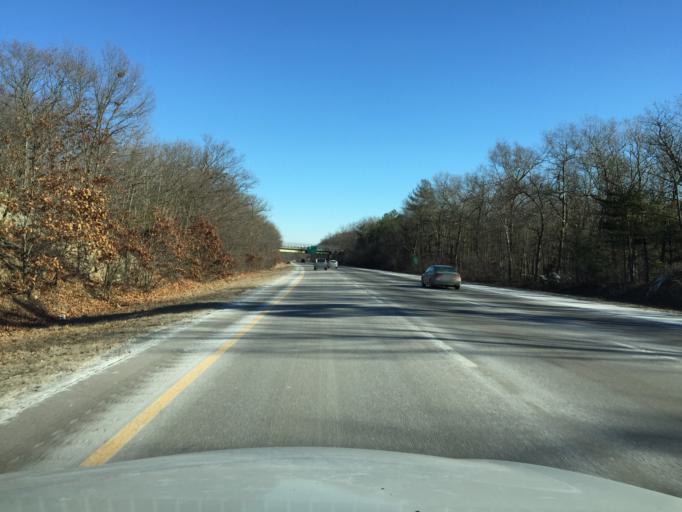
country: US
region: Massachusetts
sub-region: Norfolk County
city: Wrentham
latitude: 42.0373
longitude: -71.3245
